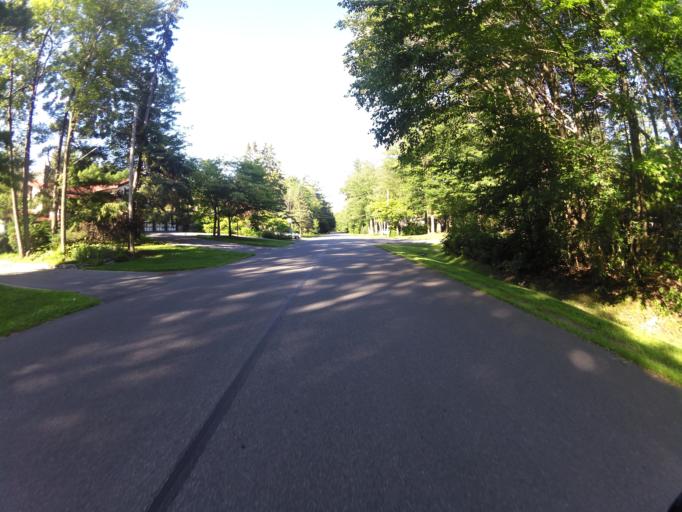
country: CA
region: Ontario
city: Ottawa
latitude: 45.3186
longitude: -75.7250
